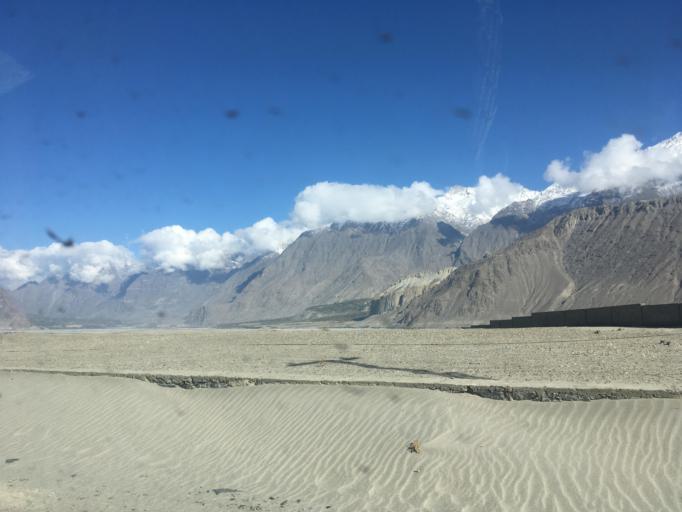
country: PK
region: Gilgit-Baltistan
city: Skardu
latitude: 35.3595
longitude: 75.5331
